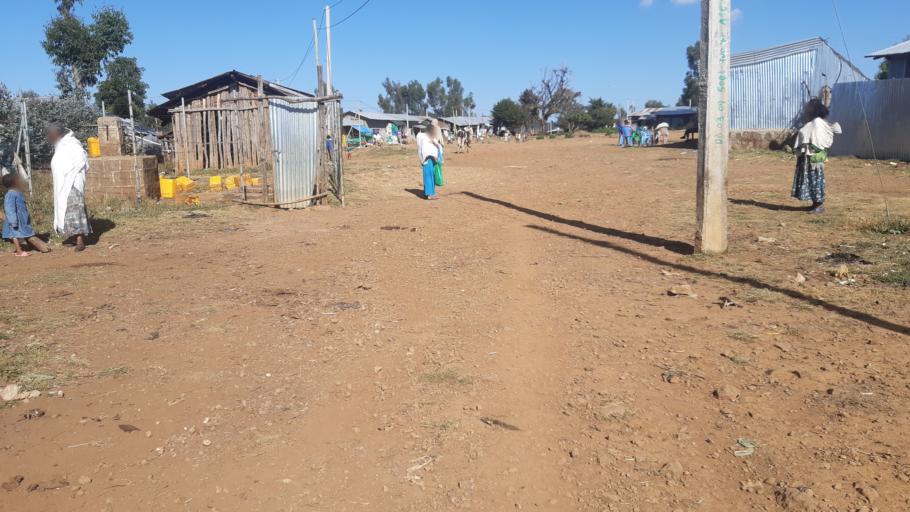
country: ET
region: Amhara
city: Dabat
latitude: 13.3510
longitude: 37.3894
